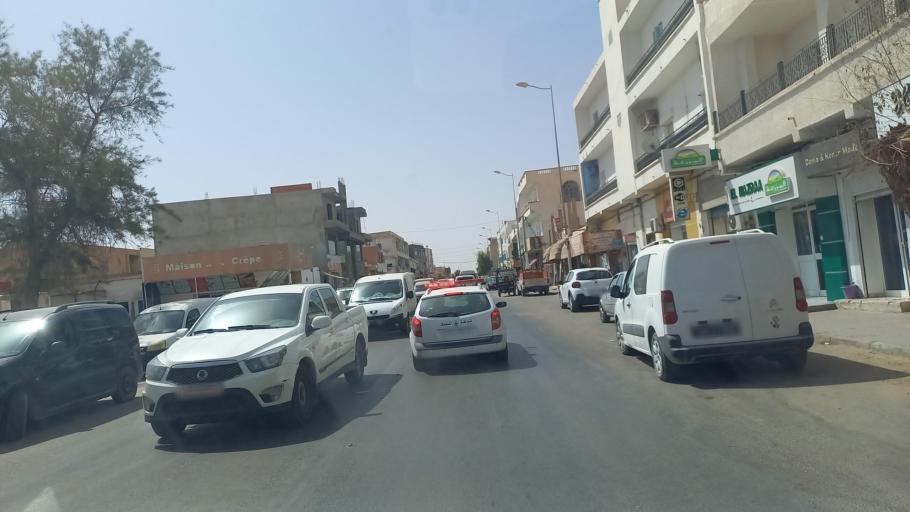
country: TN
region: Madanin
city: Medenine
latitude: 33.3346
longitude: 10.4855
